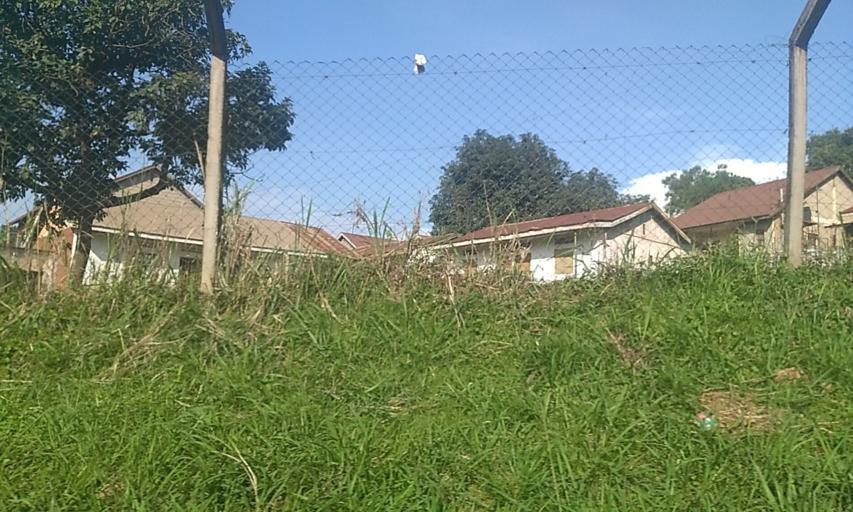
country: UG
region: Central Region
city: Kampala Central Division
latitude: 0.3150
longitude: 32.5539
